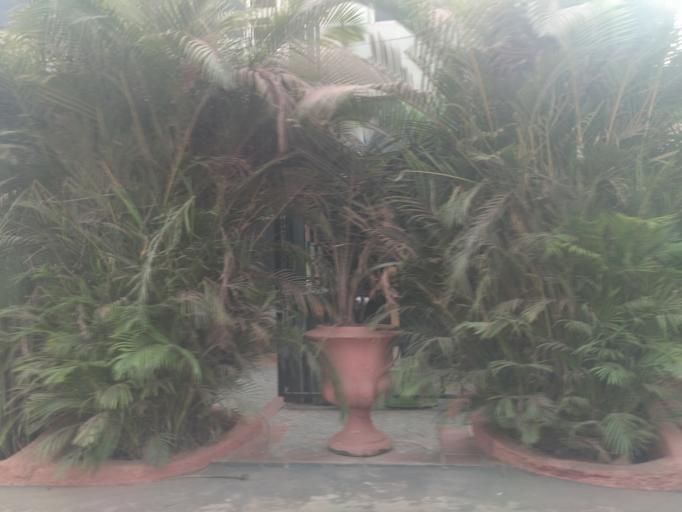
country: GH
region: Ashanti
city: Kumasi
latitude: 6.7000
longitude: -1.6309
